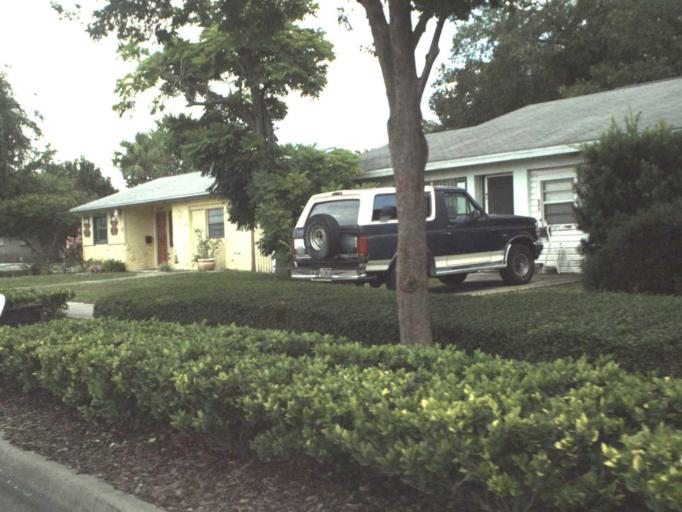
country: US
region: Florida
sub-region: Seminole County
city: Winter Springs
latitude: 28.7011
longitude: -81.2969
